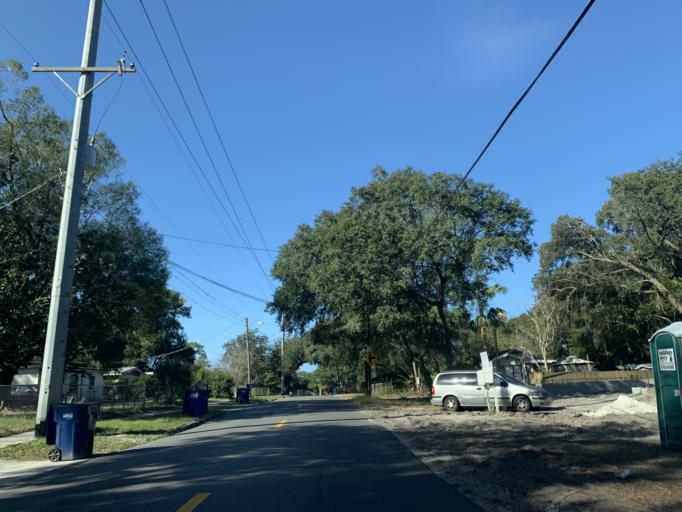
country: US
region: Florida
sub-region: Hillsborough County
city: Temple Terrace
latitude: 28.0290
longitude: -82.4131
